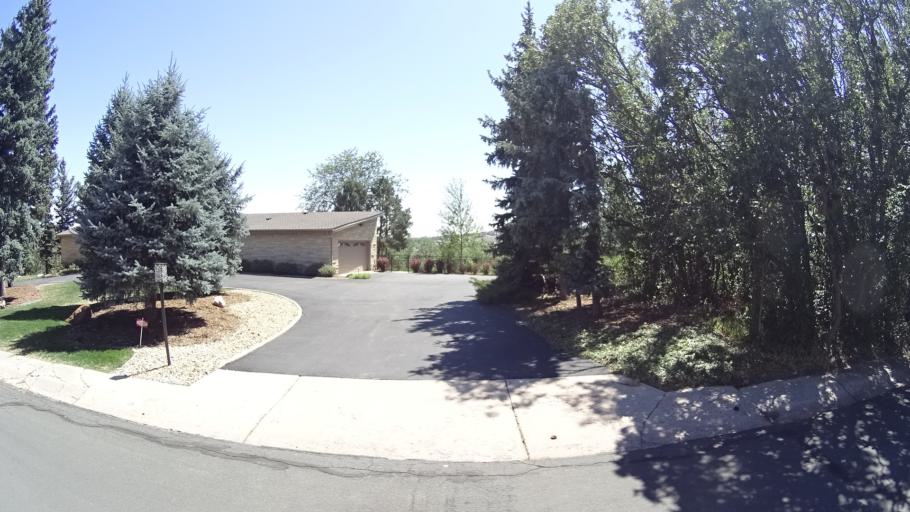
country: US
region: Colorado
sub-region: El Paso County
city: Colorado Springs
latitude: 38.7853
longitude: -104.8304
